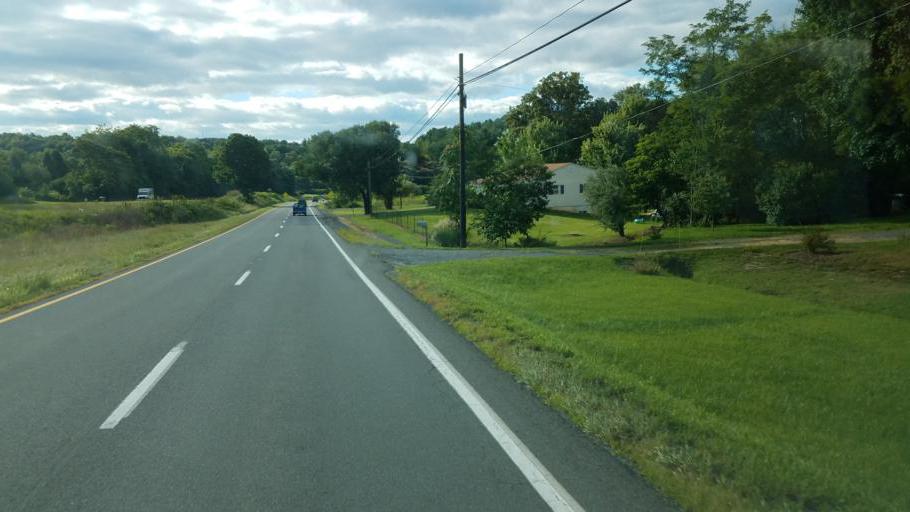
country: US
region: Virginia
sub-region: City of Winchester
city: Winchester
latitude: 39.2587
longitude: -78.2201
